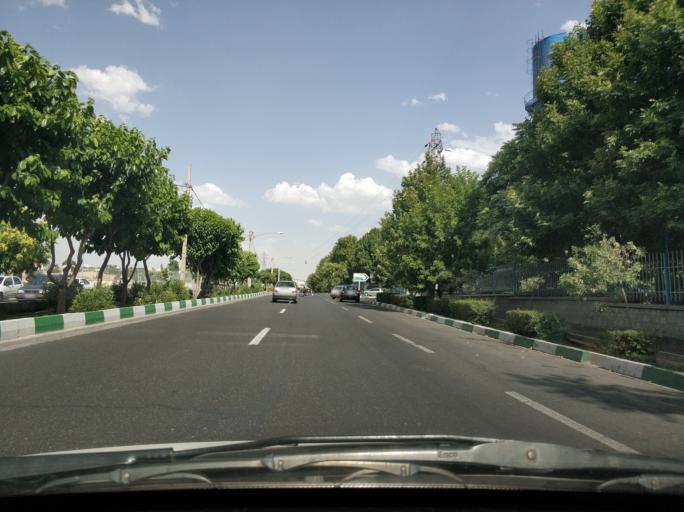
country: IR
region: Tehran
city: Tajrish
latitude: 35.7451
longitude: 51.5756
